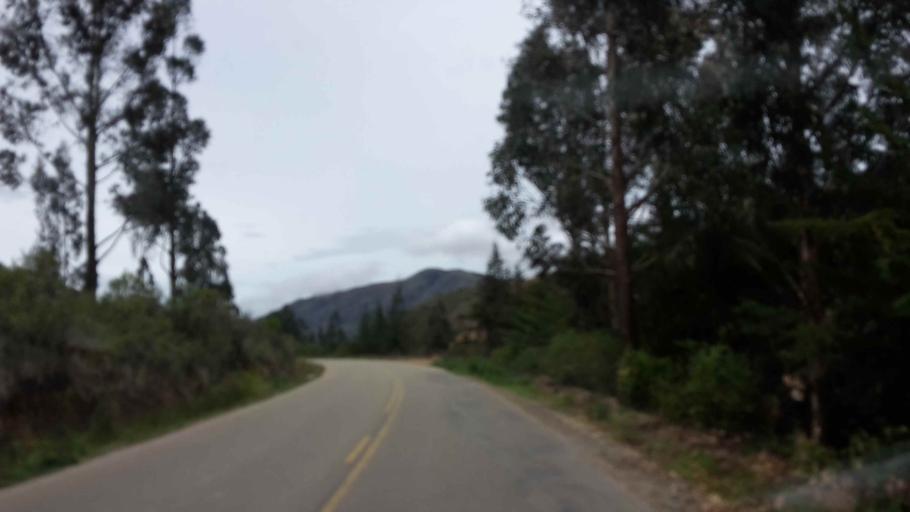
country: BO
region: Cochabamba
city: Totora
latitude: -17.6718
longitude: -65.2197
